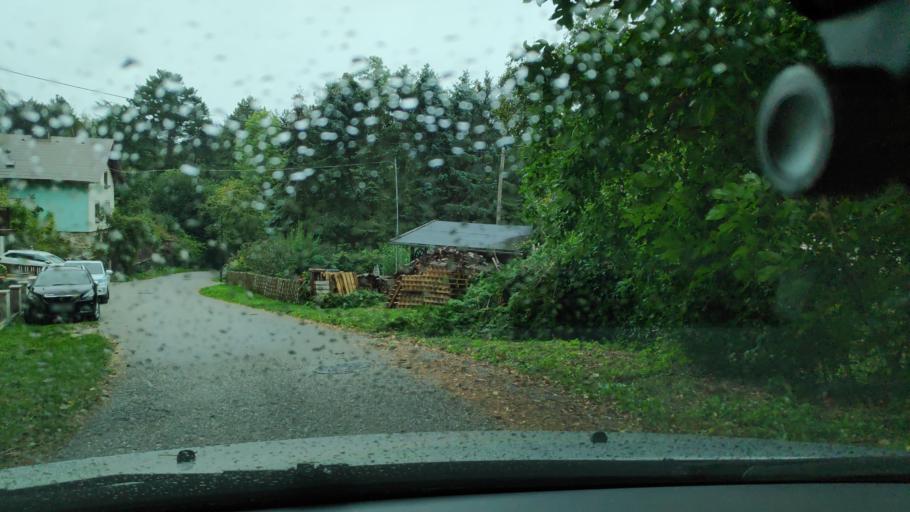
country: AT
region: Lower Austria
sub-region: Politischer Bezirk Neunkirchen
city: Grunbach am Schneeberg
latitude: 47.8044
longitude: 15.9912
